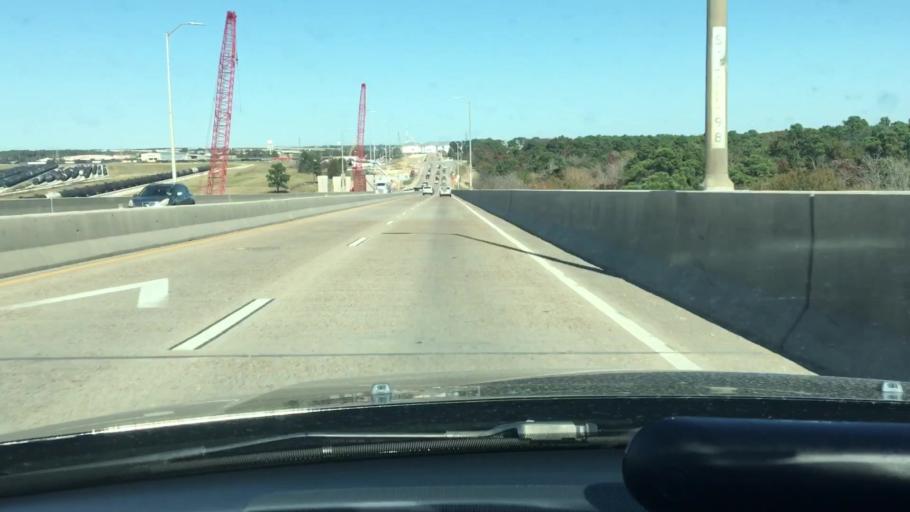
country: US
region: Texas
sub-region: Harris County
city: Deer Park
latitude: 29.7432
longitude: -95.1456
